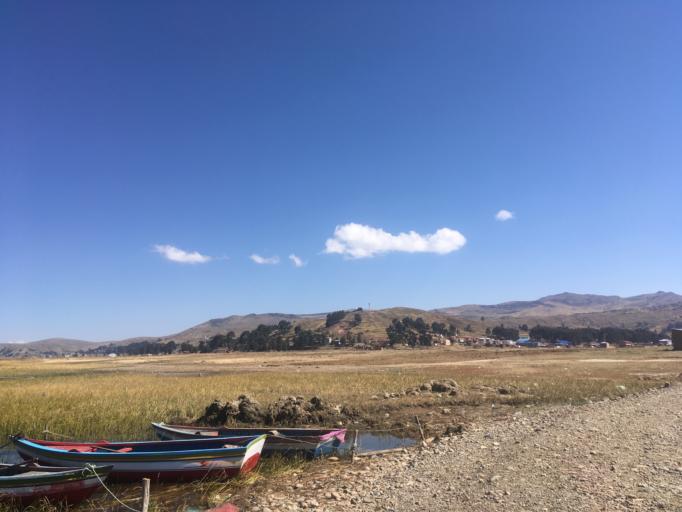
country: BO
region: La Paz
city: Huatajata
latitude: -16.2003
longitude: -68.7461
